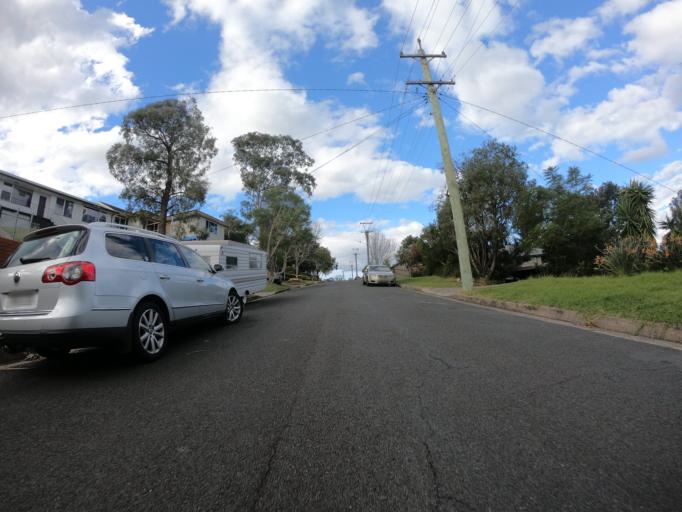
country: AU
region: New South Wales
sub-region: Wollongong
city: Mount Keira
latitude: -34.4254
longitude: 150.8566
